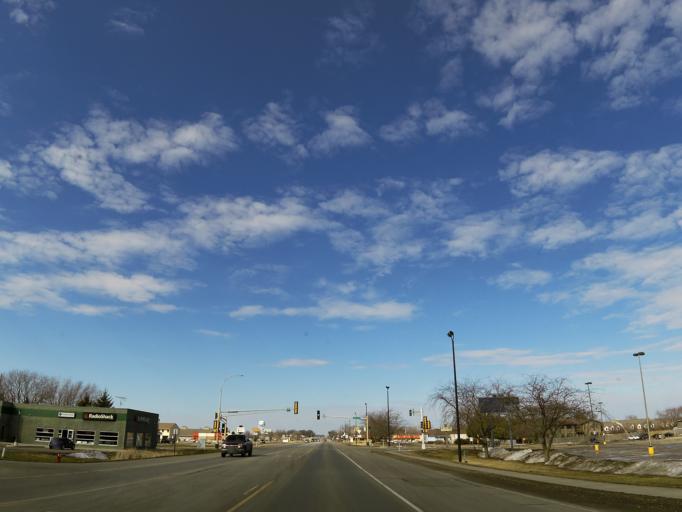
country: US
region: Minnesota
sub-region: Waseca County
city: Waseca
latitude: 44.0897
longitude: -93.5070
